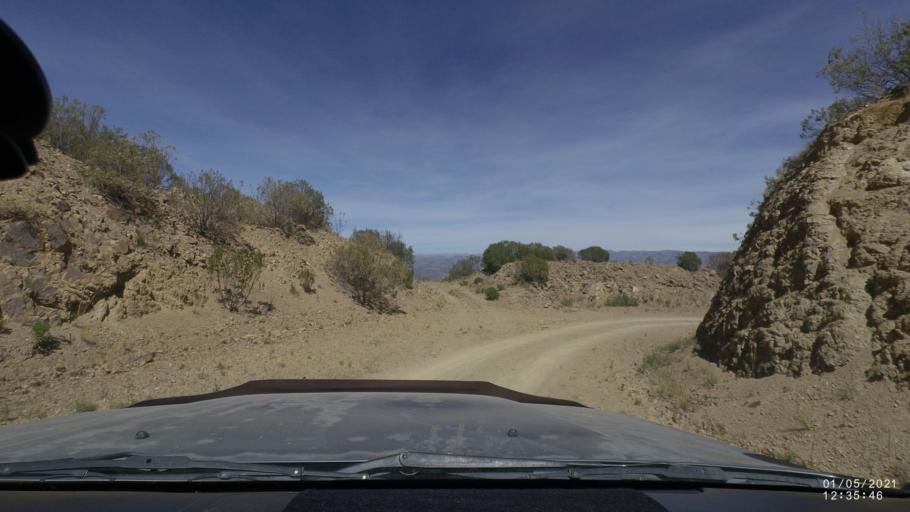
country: BO
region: Cochabamba
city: Capinota
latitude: -17.6791
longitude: -66.1535
